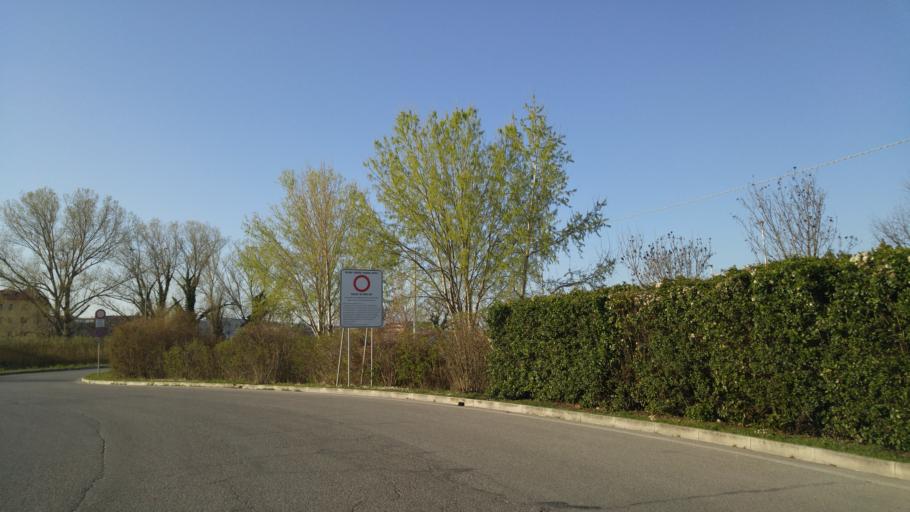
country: IT
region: The Marches
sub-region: Provincia di Pesaro e Urbino
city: Pesaro
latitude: 43.8878
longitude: 12.9077
